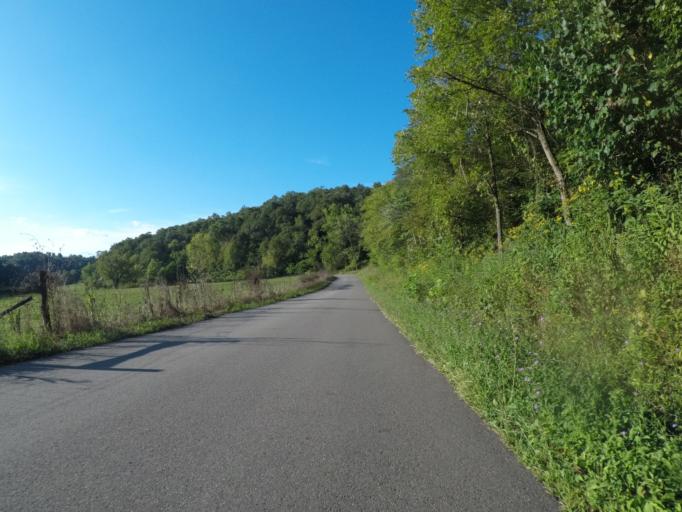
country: US
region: Ohio
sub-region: Lawrence County
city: Coal Grove
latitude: 38.5453
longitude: -82.5504
